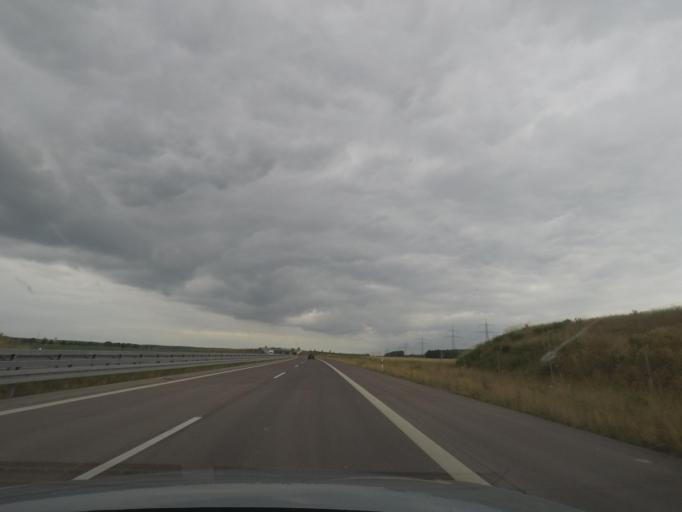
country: DE
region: Saxony-Anhalt
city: Colbitz
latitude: 52.3094
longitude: 11.6303
